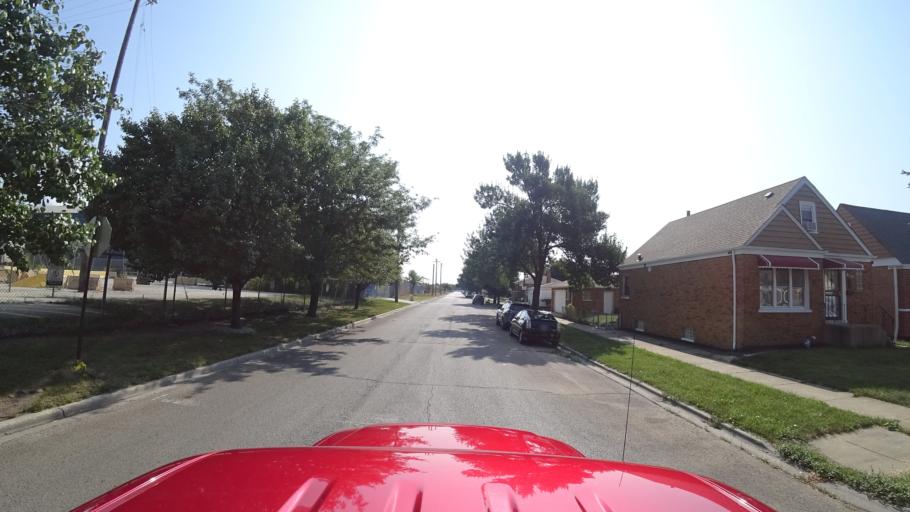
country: US
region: Illinois
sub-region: Cook County
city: Cicero
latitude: 41.8154
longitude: -87.7103
